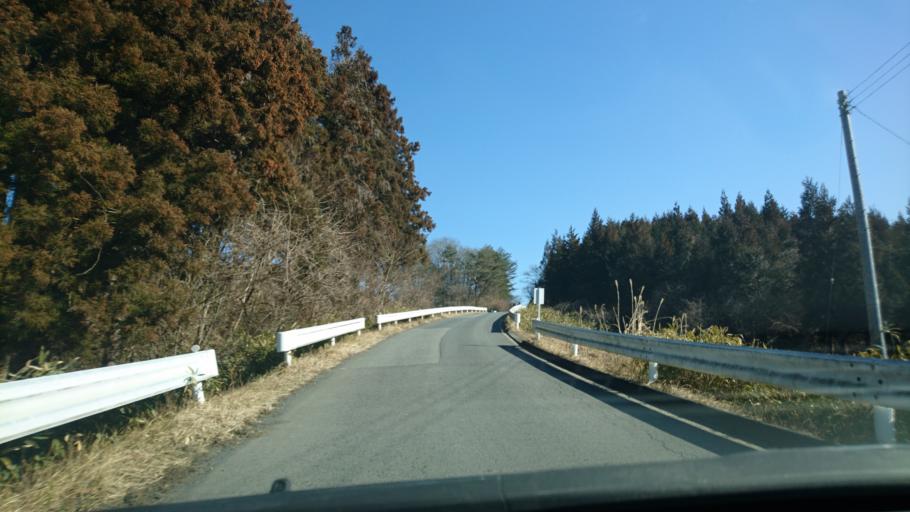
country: JP
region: Iwate
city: Ichinoseki
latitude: 38.8487
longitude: 141.2258
